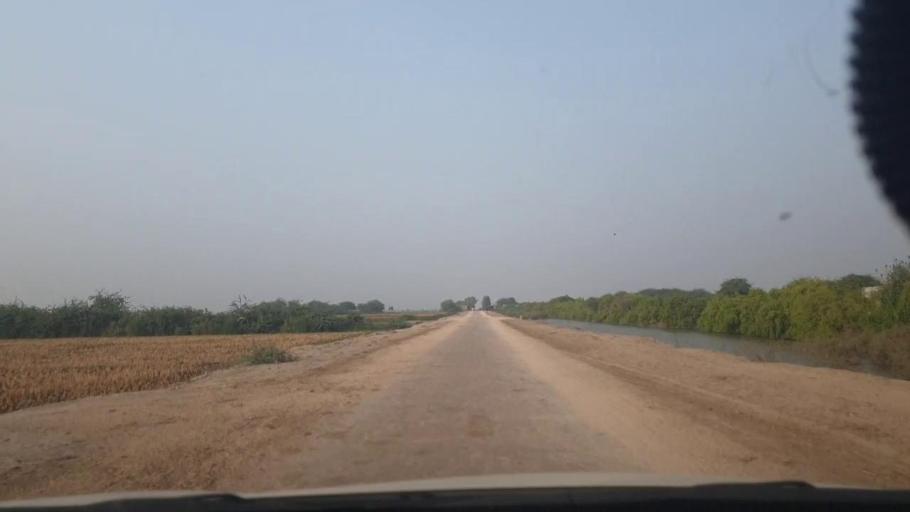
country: PK
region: Sindh
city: Bulri
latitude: 24.8340
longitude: 68.4030
